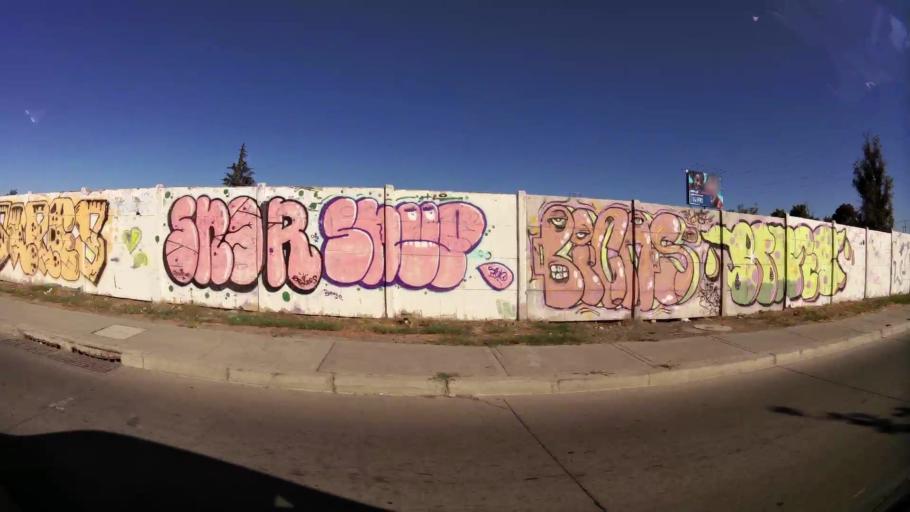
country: CL
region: O'Higgins
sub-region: Provincia de Cachapoal
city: Rancagua
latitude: -34.1838
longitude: -70.7263
